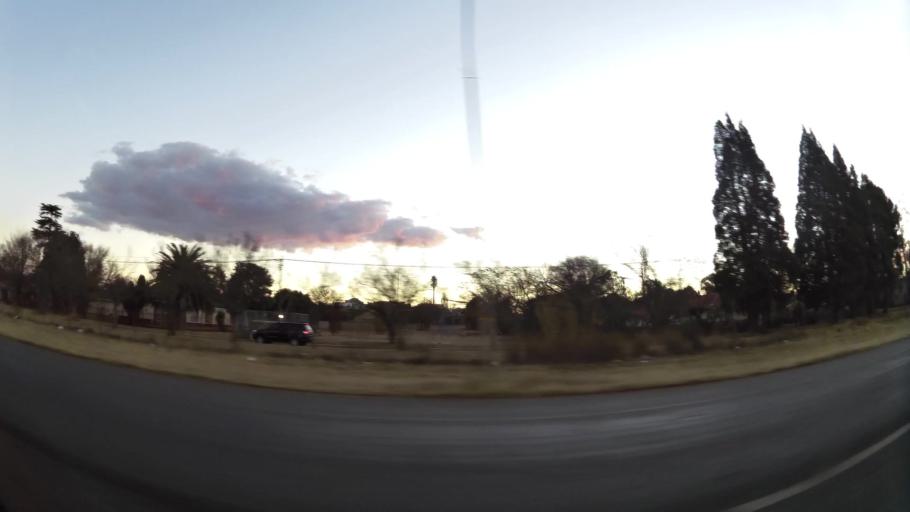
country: ZA
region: North-West
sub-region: Dr Kenneth Kaunda District Municipality
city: Potchefstroom
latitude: -26.6941
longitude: 27.0786
